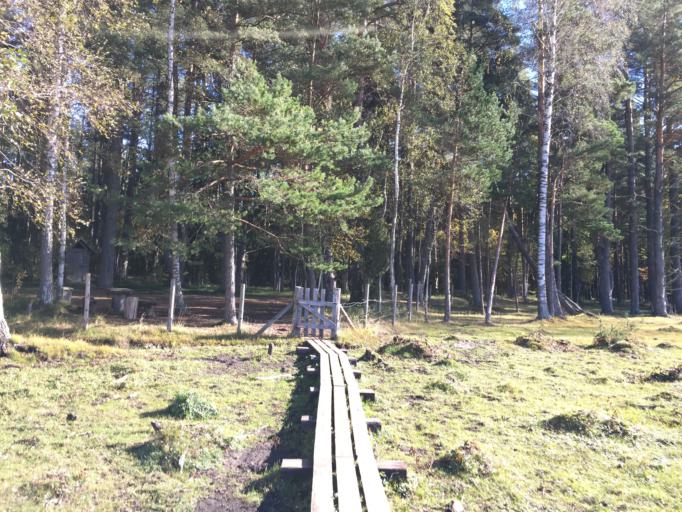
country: LV
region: Mesraga
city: Mersrags
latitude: 57.2714
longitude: 23.1314
